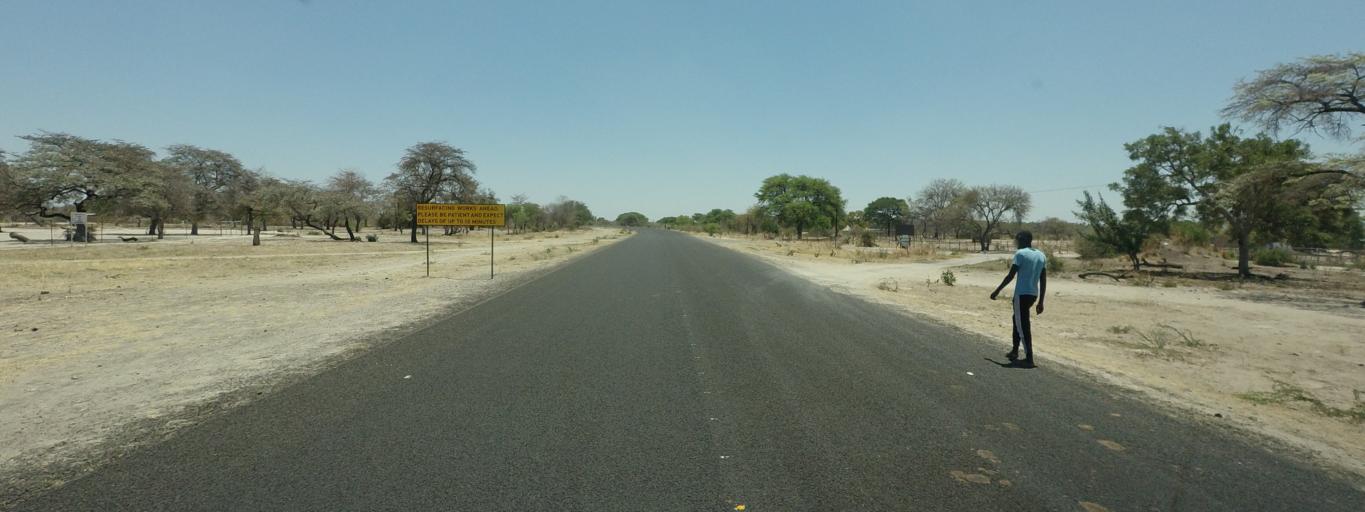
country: BW
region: North West
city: Kasane
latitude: -17.9086
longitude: 24.7065
